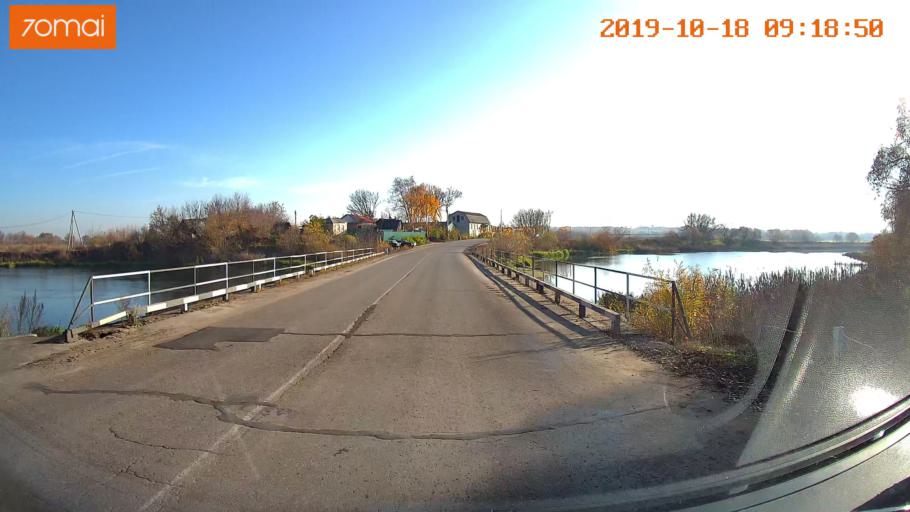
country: RU
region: Tula
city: Yefremov
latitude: 53.1350
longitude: 38.1222
